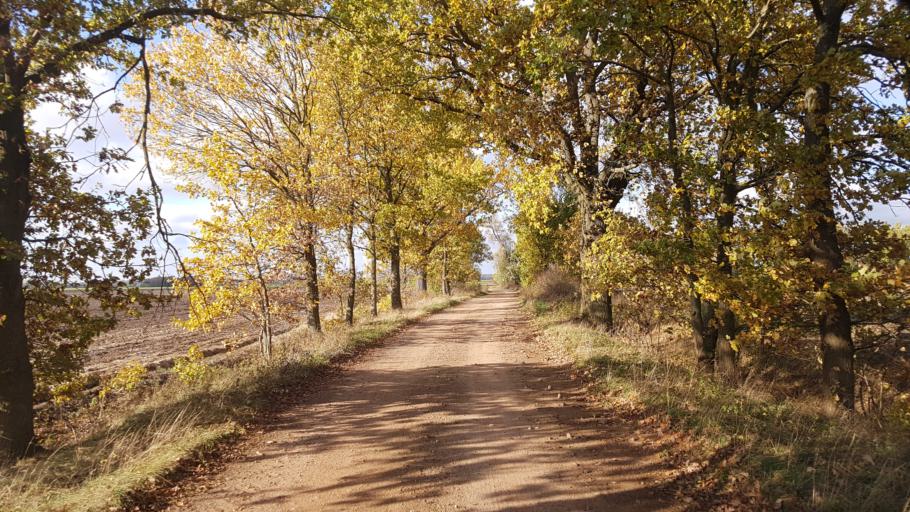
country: DE
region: Brandenburg
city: Schonewalde
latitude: 51.6820
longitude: 13.5822
